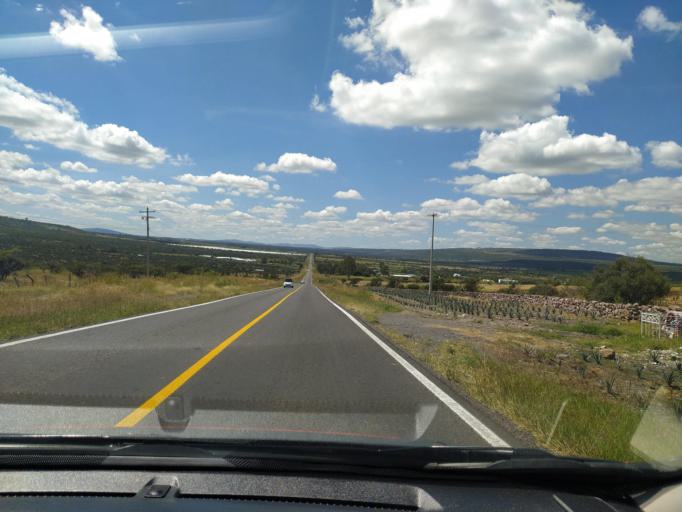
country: MX
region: Jalisco
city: San Miguel el Alto
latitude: 21.0237
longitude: -102.4358
